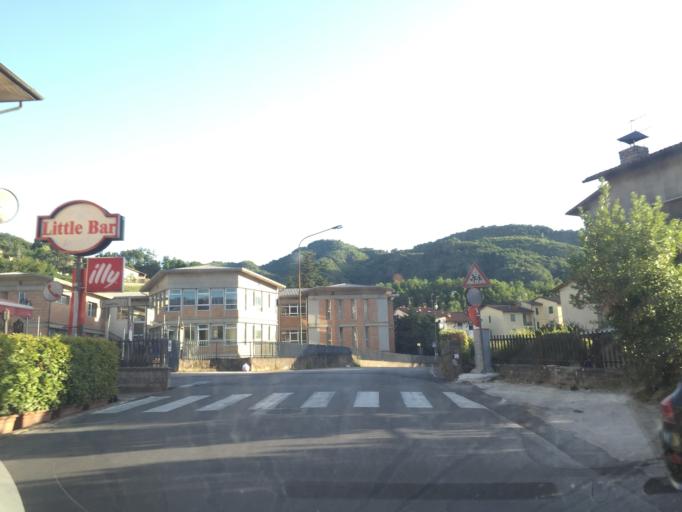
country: IT
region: Tuscany
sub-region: Provincia di Lucca
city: Castelnuovo di Garfagnana
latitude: 44.1046
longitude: 10.4080
